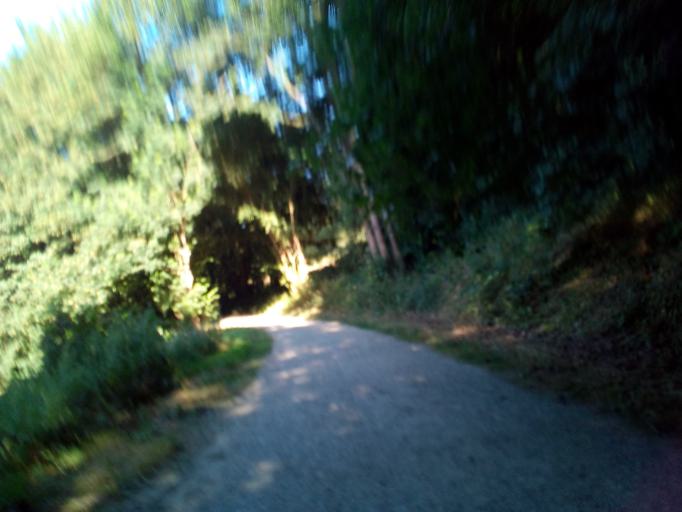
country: FR
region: Brittany
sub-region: Departement du Finistere
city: Landivisiau
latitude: 48.5058
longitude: -4.0817
